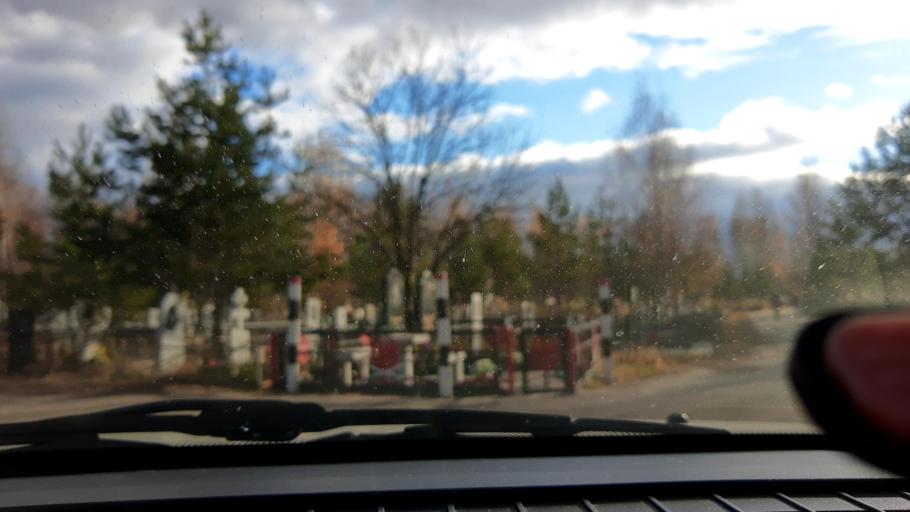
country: RU
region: Nizjnij Novgorod
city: Gorbatovka
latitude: 56.3602
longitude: 43.7705
